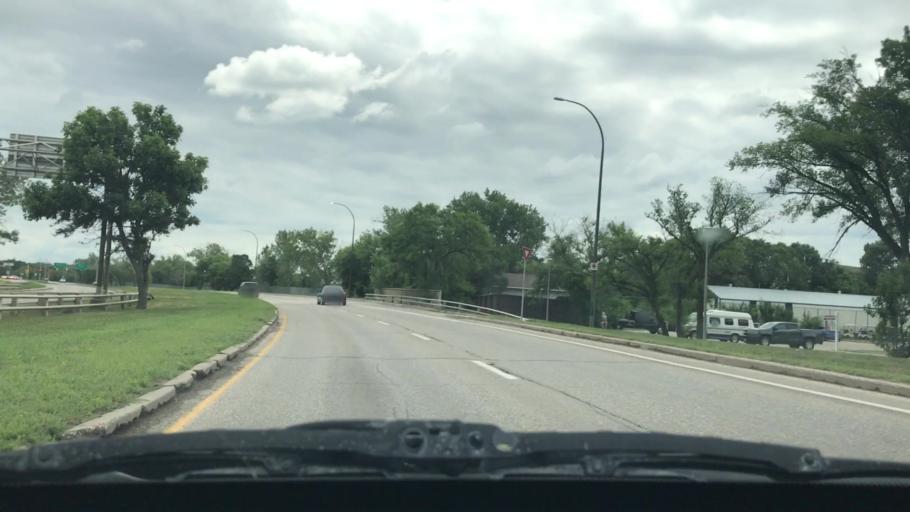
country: CA
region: Manitoba
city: Winnipeg
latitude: 49.8529
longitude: -97.1250
